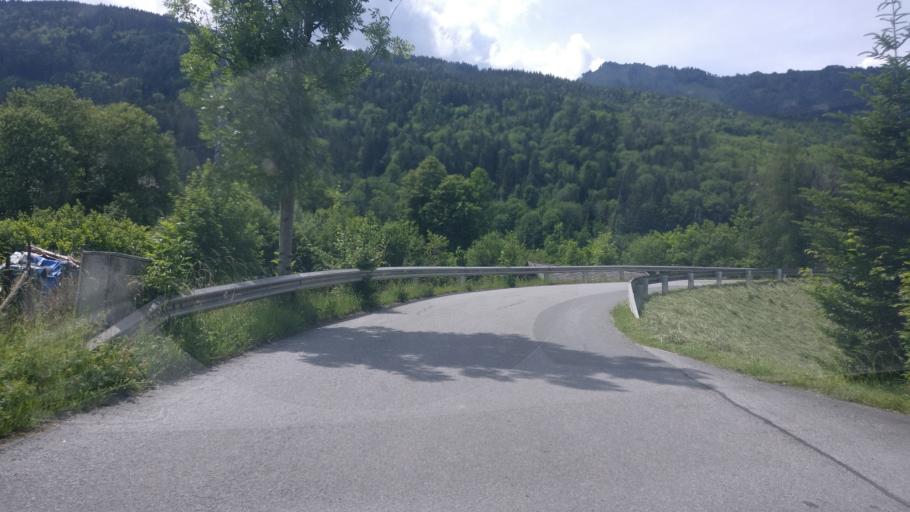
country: AT
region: Salzburg
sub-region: Politischer Bezirk Hallein
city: Kuchl
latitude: 47.6308
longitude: 13.1332
